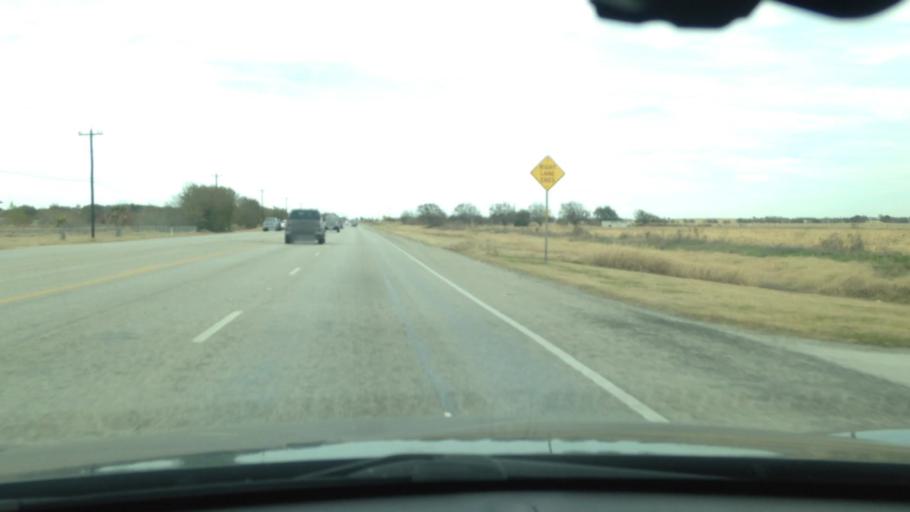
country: US
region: Texas
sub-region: Caldwell County
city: Martindale
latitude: 29.9031
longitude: -97.8673
